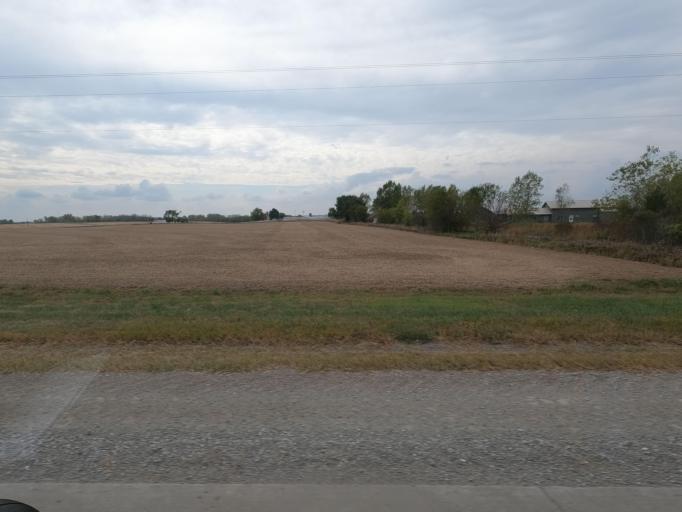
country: US
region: Iowa
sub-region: Jasper County
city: Monroe
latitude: 41.4471
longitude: -93.0221
